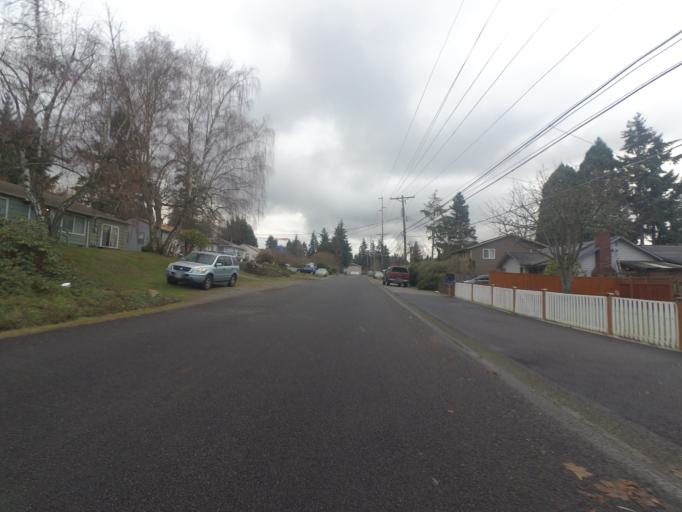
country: US
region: Washington
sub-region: Pierce County
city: University Place
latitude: 47.2296
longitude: -122.5391
